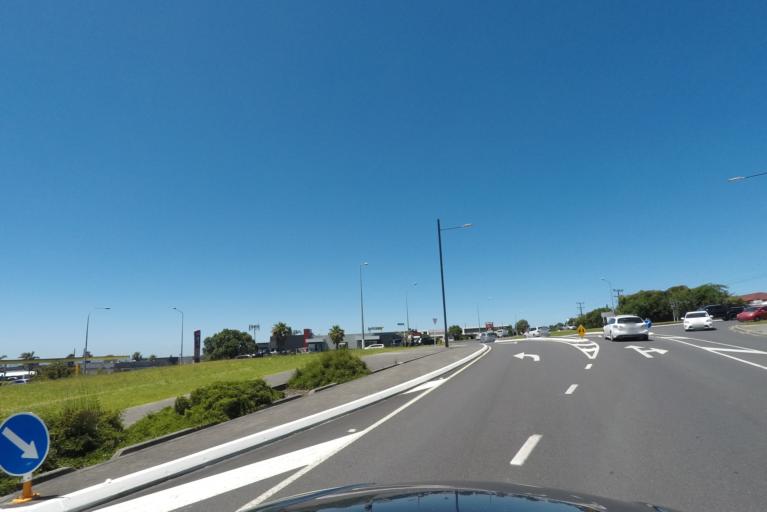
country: NZ
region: Auckland
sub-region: Auckland
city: Rosebank
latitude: -36.8209
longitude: 174.6073
